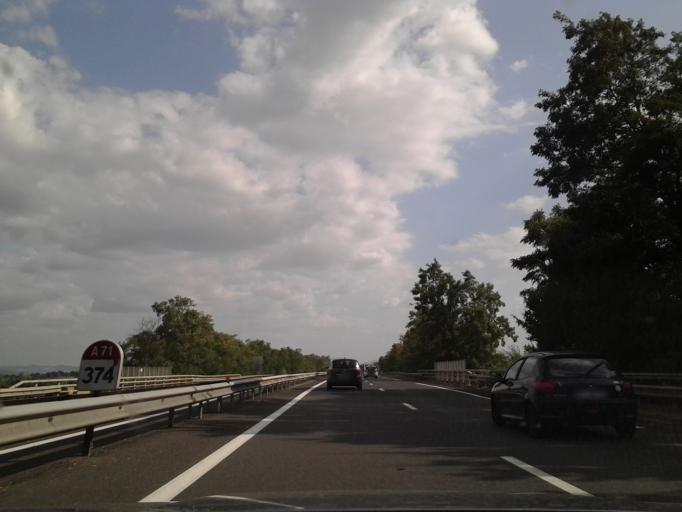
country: FR
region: Auvergne
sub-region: Departement du Puy-de-Dome
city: Riom
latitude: 45.9035
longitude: 3.1545
